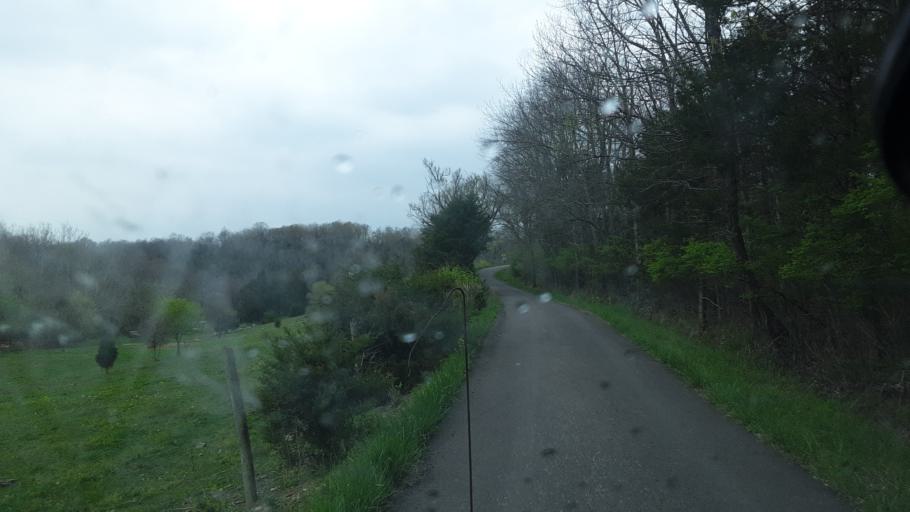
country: US
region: Kentucky
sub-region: Owen County
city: Owenton
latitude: 38.6724
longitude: -84.7961
